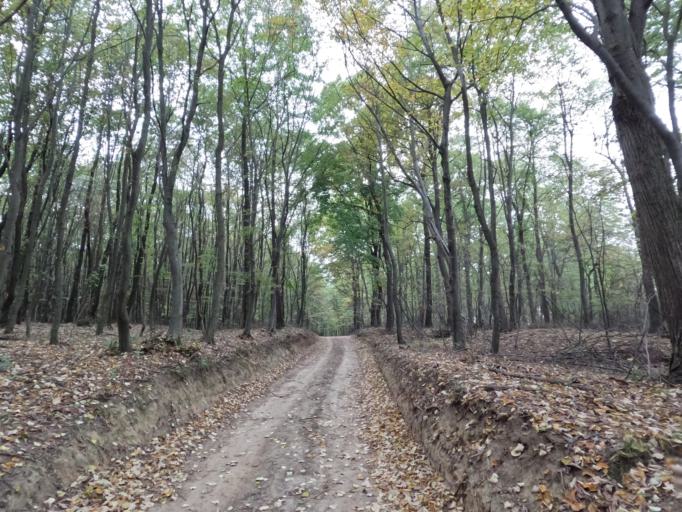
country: HU
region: Tolna
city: Szentgalpuszta
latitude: 46.3185
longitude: 18.6344
